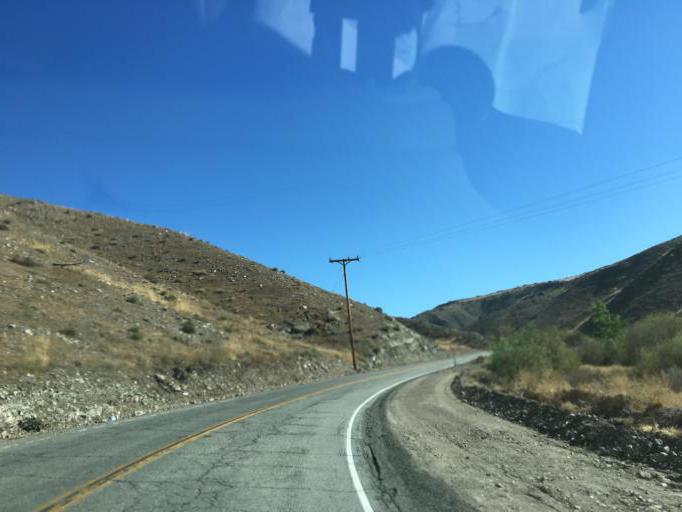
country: US
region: California
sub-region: Los Angeles County
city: Agua Dulce
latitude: 34.4719
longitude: -118.3318
